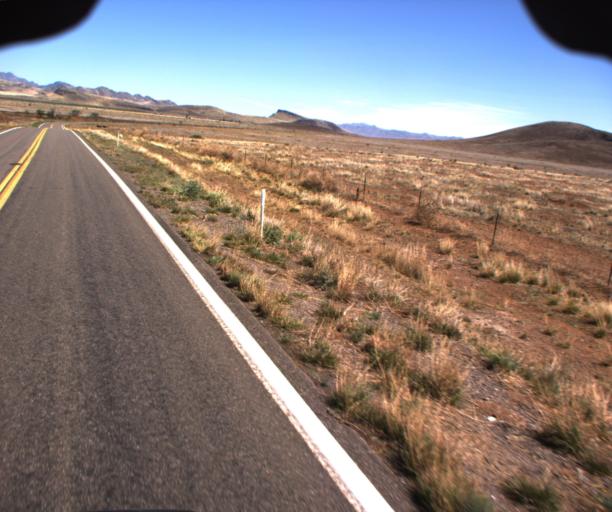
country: US
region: Arizona
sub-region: Cochise County
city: Douglas
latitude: 31.6164
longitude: -109.2154
